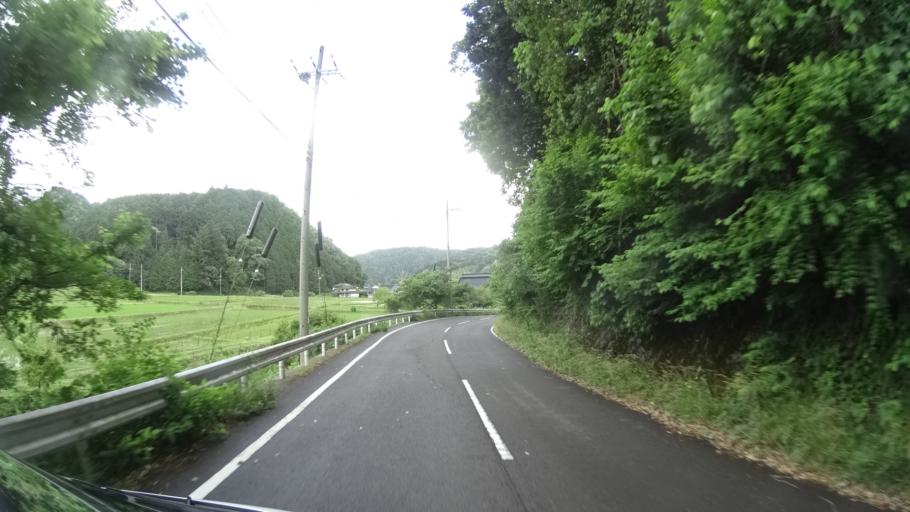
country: JP
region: Kyoto
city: Ayabe
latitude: 35.3821
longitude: 135.2135
